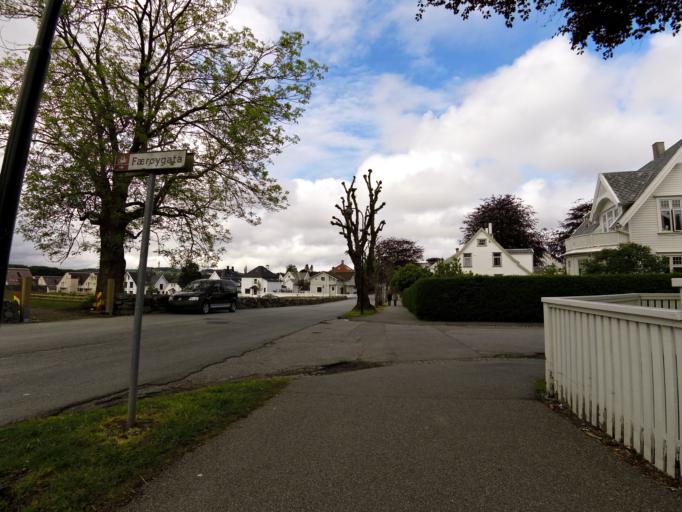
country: NO
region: Rogaland
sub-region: Stavanger
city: Stavanger
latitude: 58.9648
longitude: 5.7181
